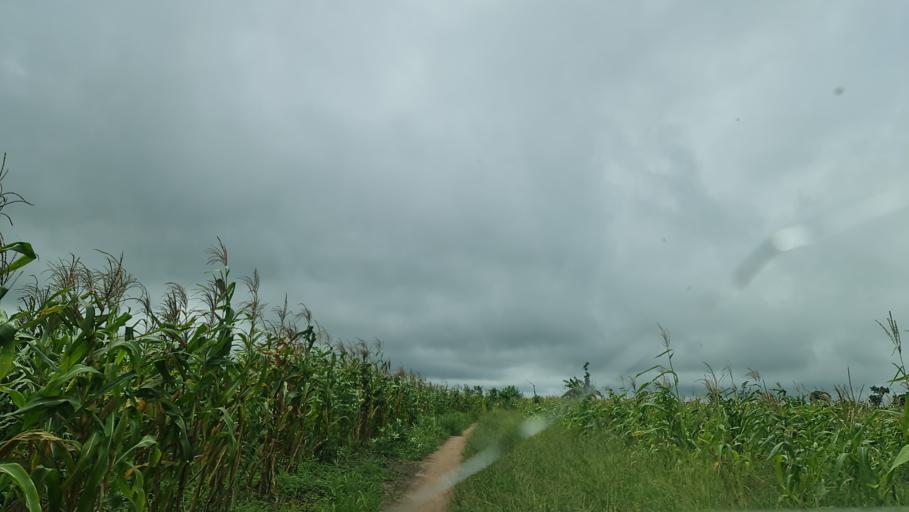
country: MW
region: Southern Region
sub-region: Nsanje District
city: Nsanje
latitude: -17.3415
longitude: 35.7326
